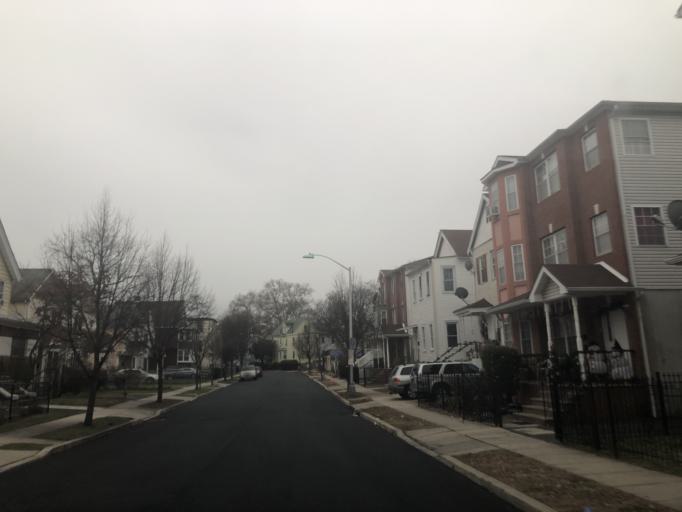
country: US
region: New Jersey
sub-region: Essex County
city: Orange
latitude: 40.7591
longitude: -74.2233
